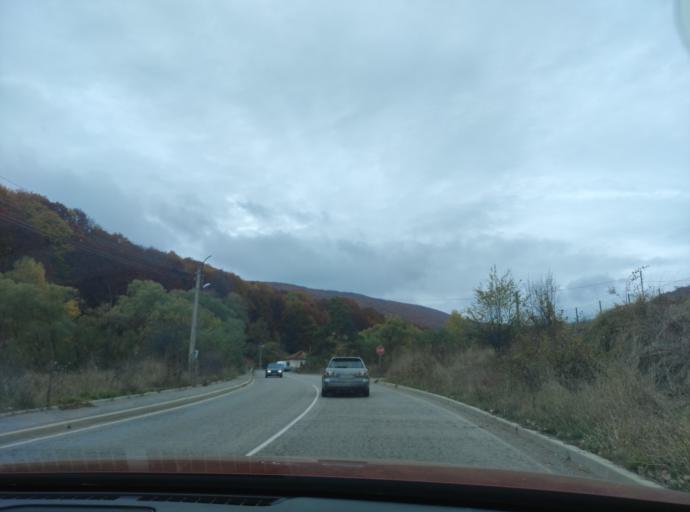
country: BG
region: Sofiya
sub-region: Obshtina Godech
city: Godech
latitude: 43.0812
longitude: 23.1057
